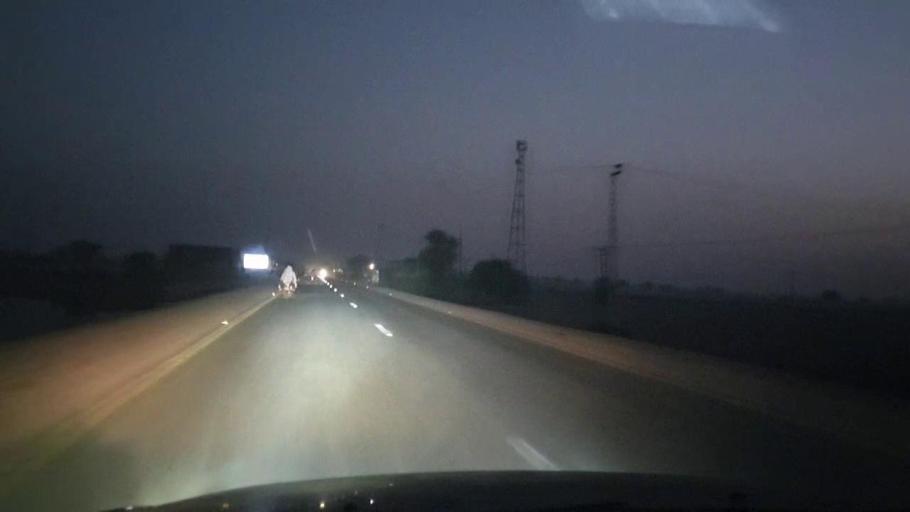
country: PK
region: Sindh
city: Chambar
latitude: 25.3333
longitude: 68.7972
